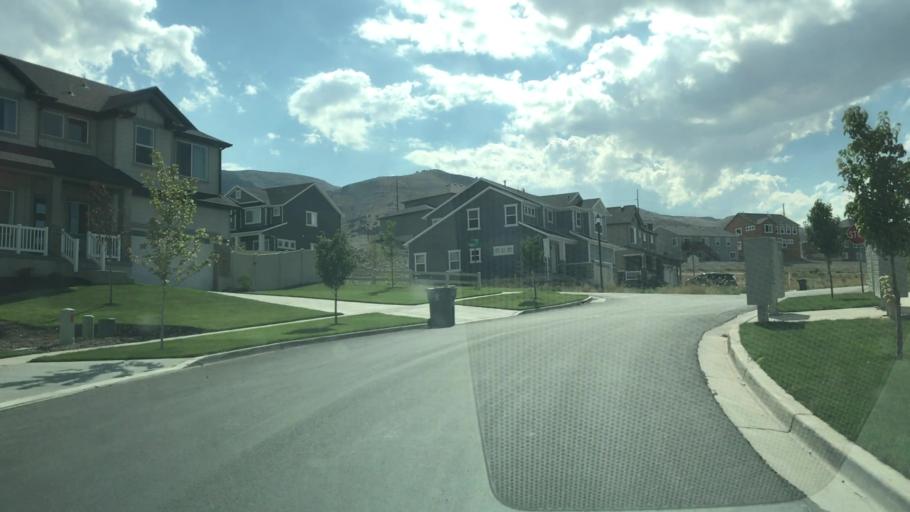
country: US
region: Utah
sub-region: Utah County
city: Saratoga Springs
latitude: 40.3037
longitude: -111.9006
